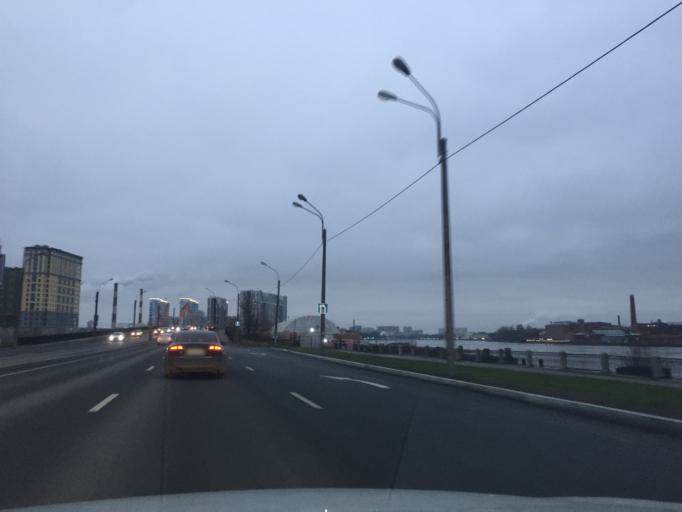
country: RU
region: St.-Petersburg
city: Obukhovo
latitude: 59.9021
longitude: 30.4395
